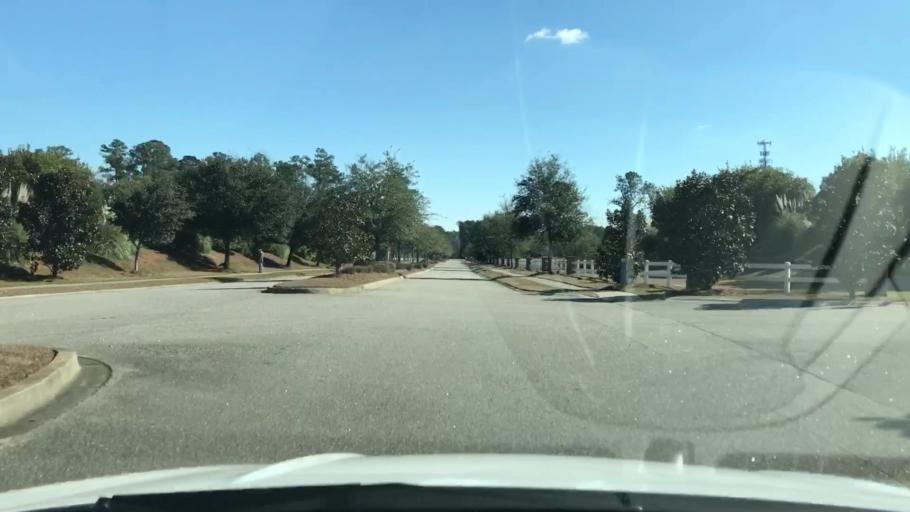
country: US
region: South Carolina
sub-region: Horry County
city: Socastee
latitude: 33.6430
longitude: -79.0352
